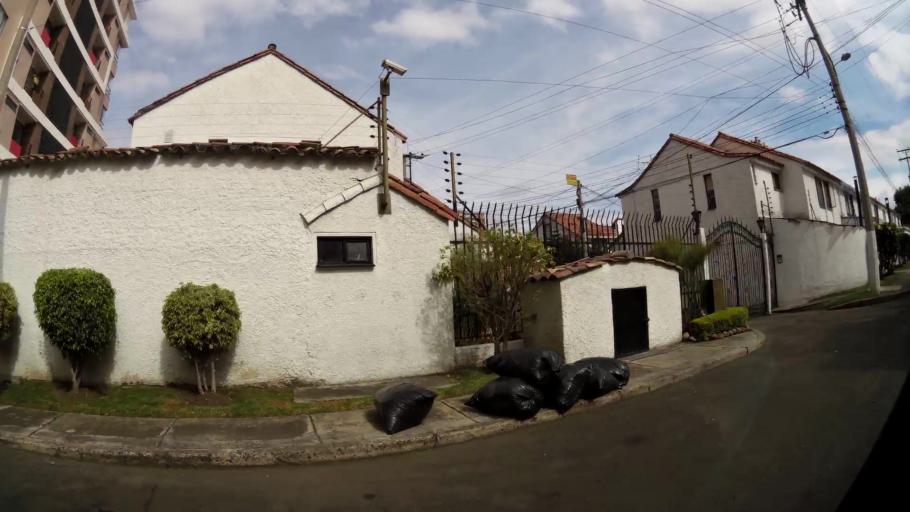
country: CO
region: Bogota D.C.
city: Barrio San Luis
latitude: 4.7241
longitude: -74.0311
